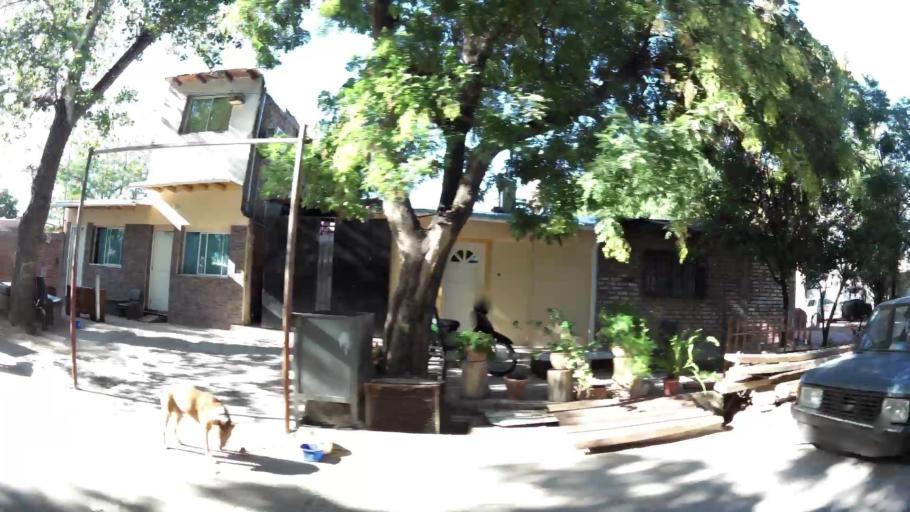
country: AR
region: Mendoza
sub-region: Departamento de Godoy Cruz
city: Godoy Cruz
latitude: -32.9222
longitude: -68.8569
